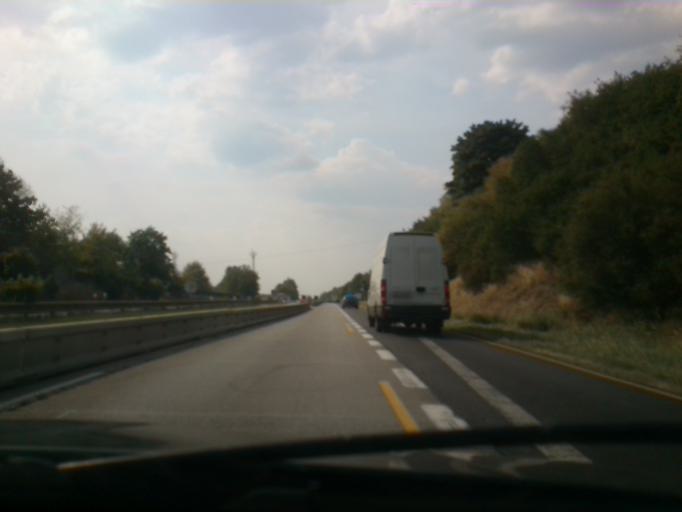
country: CZ
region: Central Bohemia
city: Divisov
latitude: 49.8378
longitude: 14.8340
